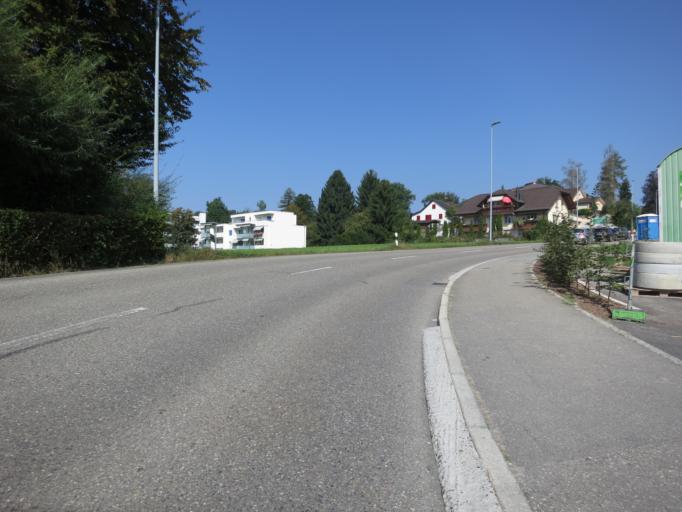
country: CH
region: Zurich
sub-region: Bezirk Meilen
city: Hombrechtikon
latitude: 47.2506
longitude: 8.7793
